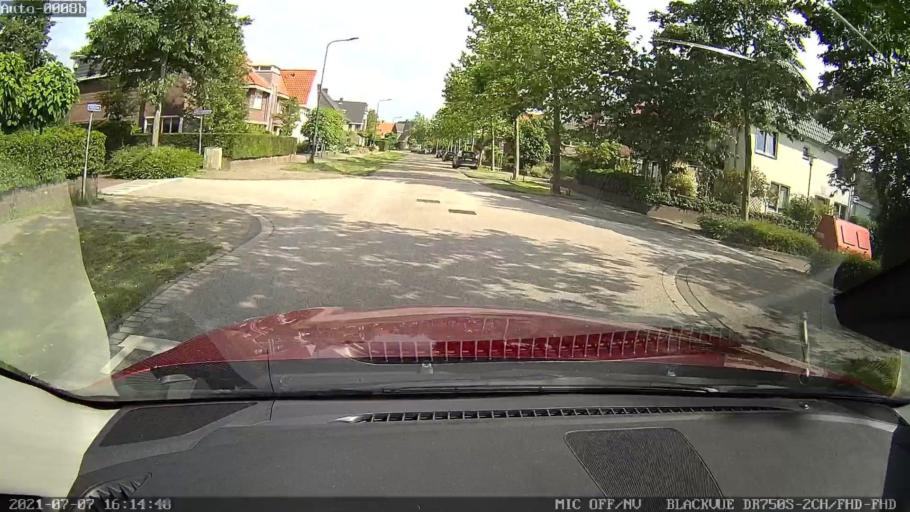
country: NL
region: Zeeland
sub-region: Gemeente Middelburg
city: Middelburg
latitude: 51.4835
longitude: 3.6356
